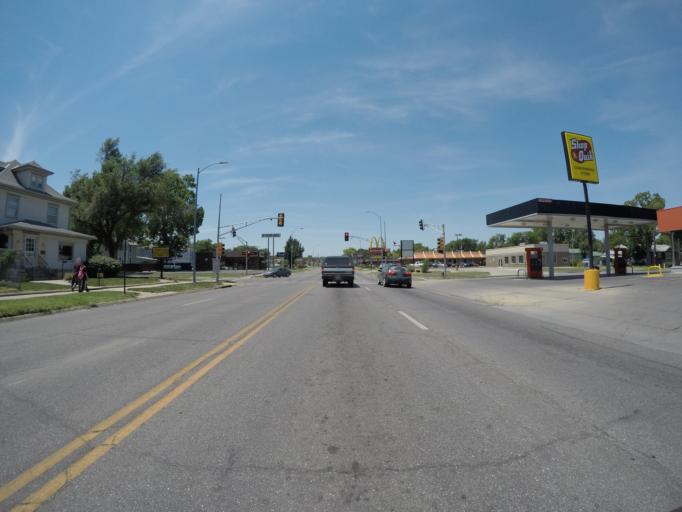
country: US
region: Kansas
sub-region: Geary County
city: Junction City
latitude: 39.0283
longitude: -96.8348
